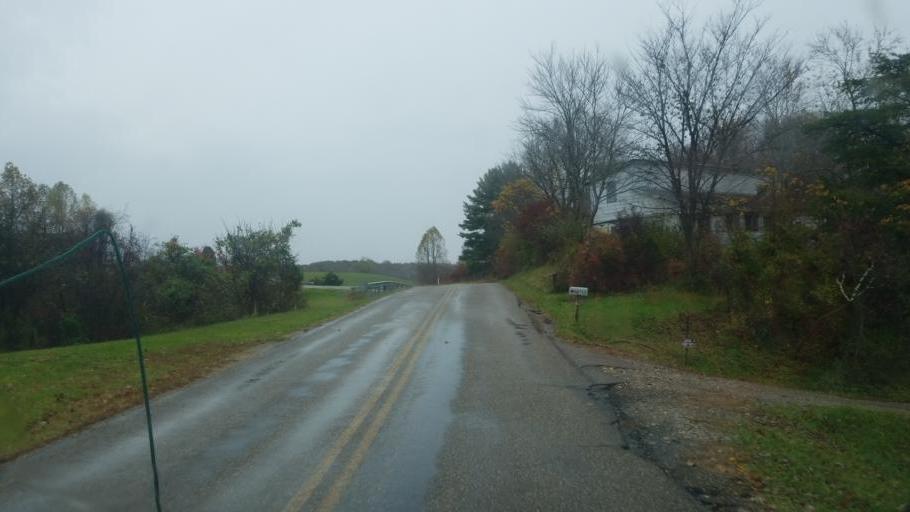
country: US
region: West Virginia
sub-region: Wood County
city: Vienna
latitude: 39.3449
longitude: -81.6270
